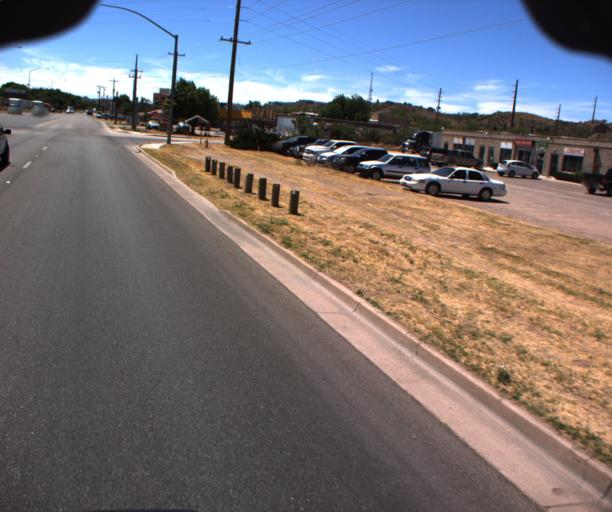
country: US
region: Arizona
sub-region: Santa Cruz County
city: Nogales
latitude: 31.3803
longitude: -110.9437
